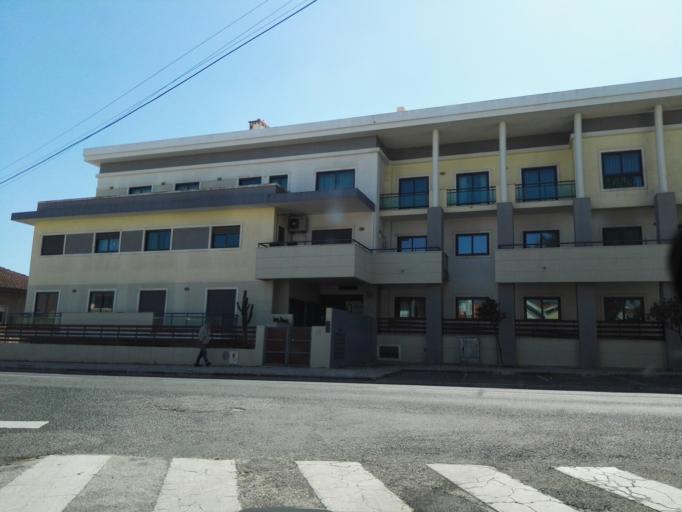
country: PT
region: Lisbon
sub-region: Sintra
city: Rio de Mouro
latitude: 38.7960
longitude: -9.3486
